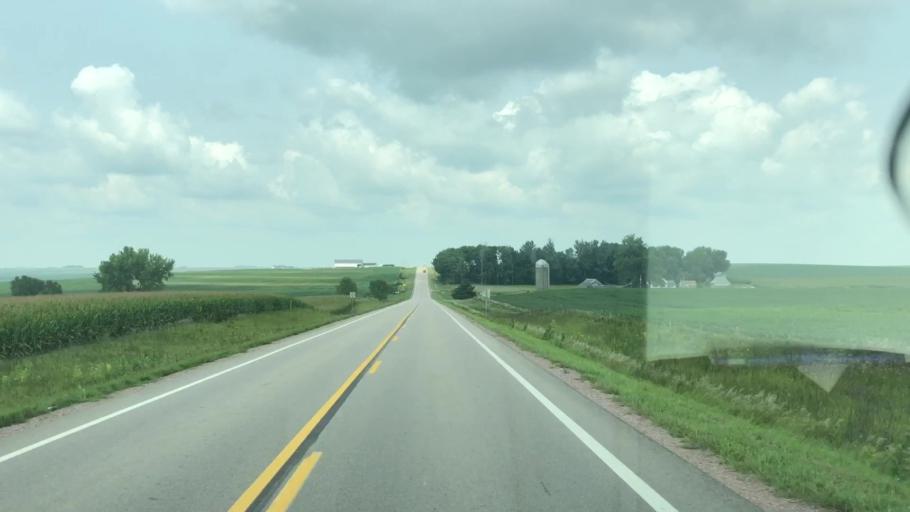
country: US
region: Iowa
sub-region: Plymouth County
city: Kingsley
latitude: 42.5950
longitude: -95.9573
